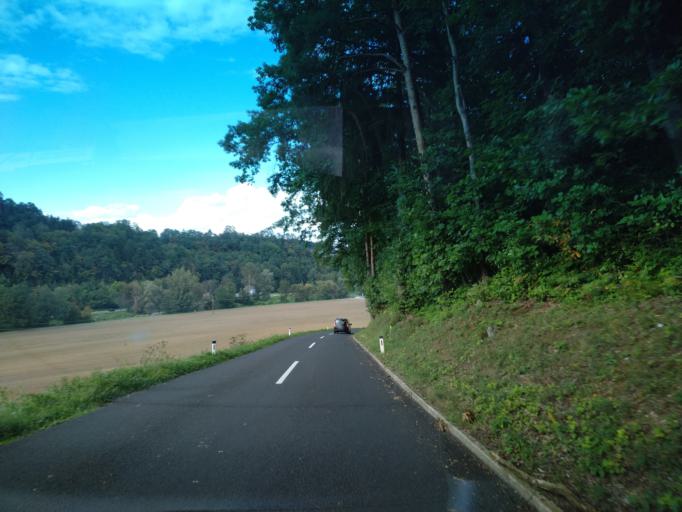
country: AT
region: Styria
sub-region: Politischer Bezirk Leibnitz
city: Leibnitz
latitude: 46.7870
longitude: 15.5223
